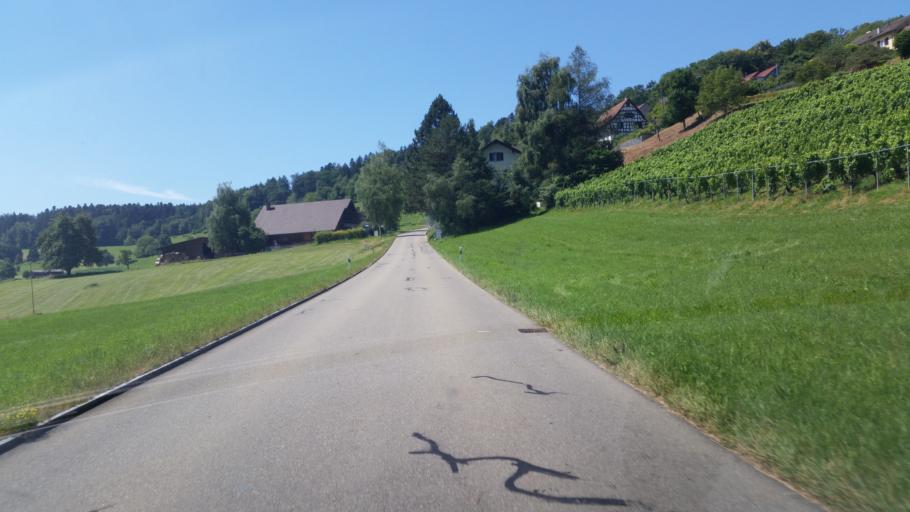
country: CH
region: Zurich
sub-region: Bezirk Dielsdorf
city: Dielsdorf
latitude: 47.4813
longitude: 8.4389
